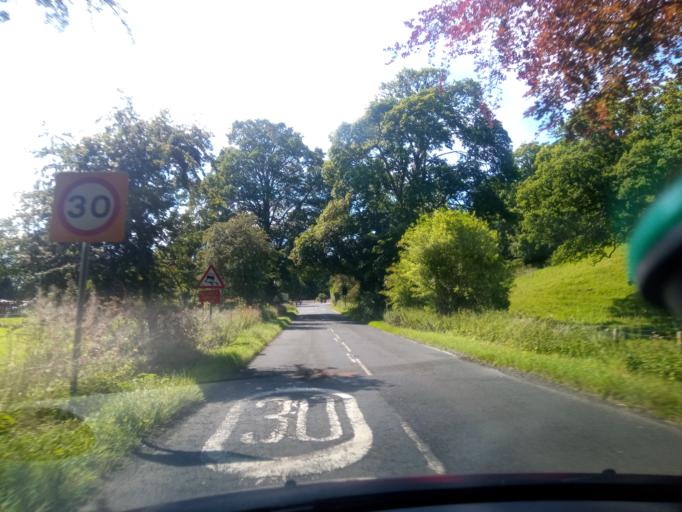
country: GB
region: England
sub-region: Northumberland
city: Bardon Mill
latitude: 54.9117
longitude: -2.3421
